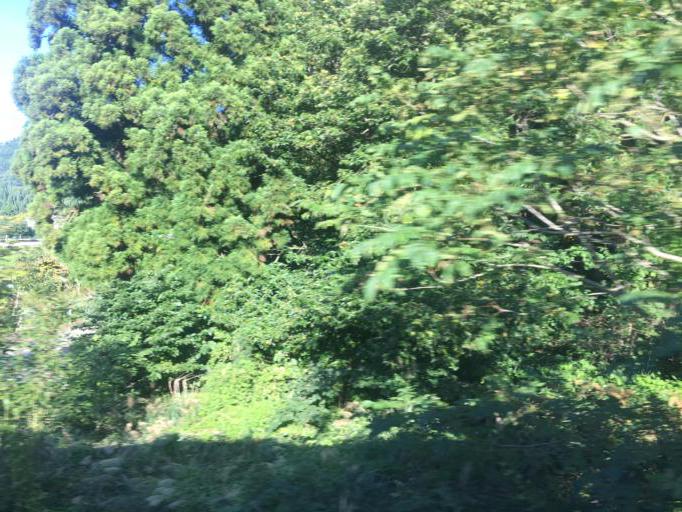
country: JP
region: Akita
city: Takanosu
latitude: 39.9932
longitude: 140.4016
